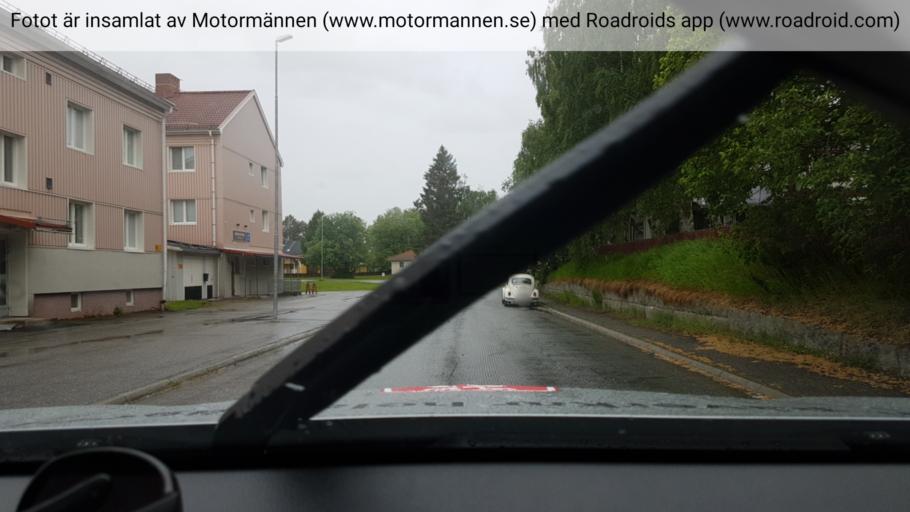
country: SE
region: Vaesterbotten
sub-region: Sorsele Kommun
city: Sorsele
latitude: 65.5359
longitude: 17.5417
